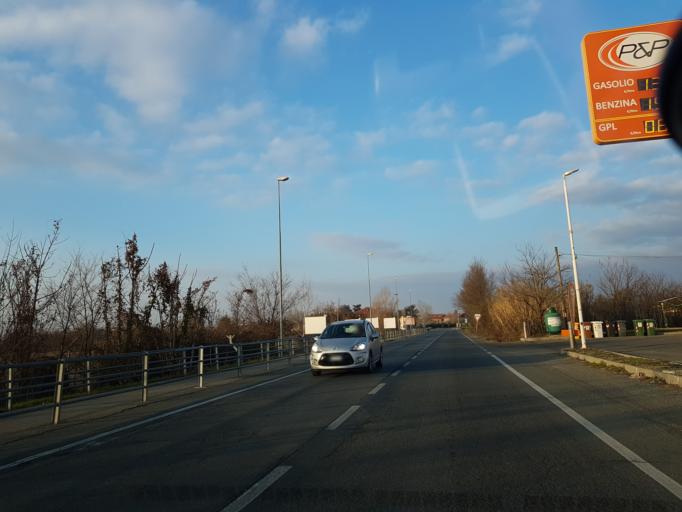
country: IT
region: Piedmont
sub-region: Provincia di Alessandria
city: Pozzolo Formigaro
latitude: 44.7841
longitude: 8.7889
